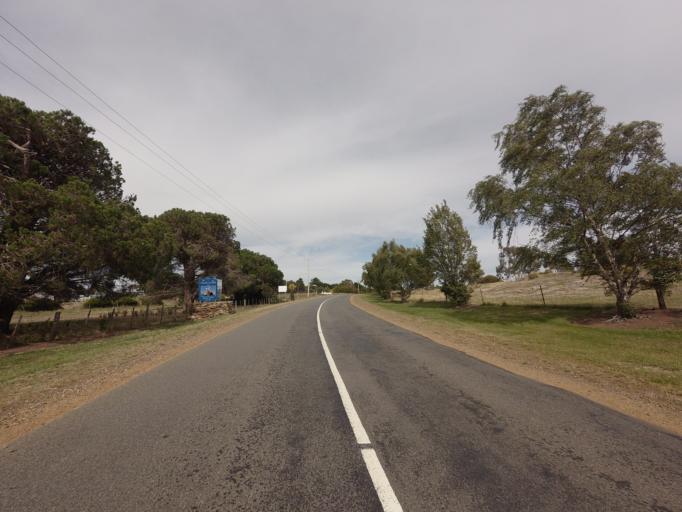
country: AU
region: Tasmania
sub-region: Brighton
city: Bridgewater
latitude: -42.2970
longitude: 147.3829
